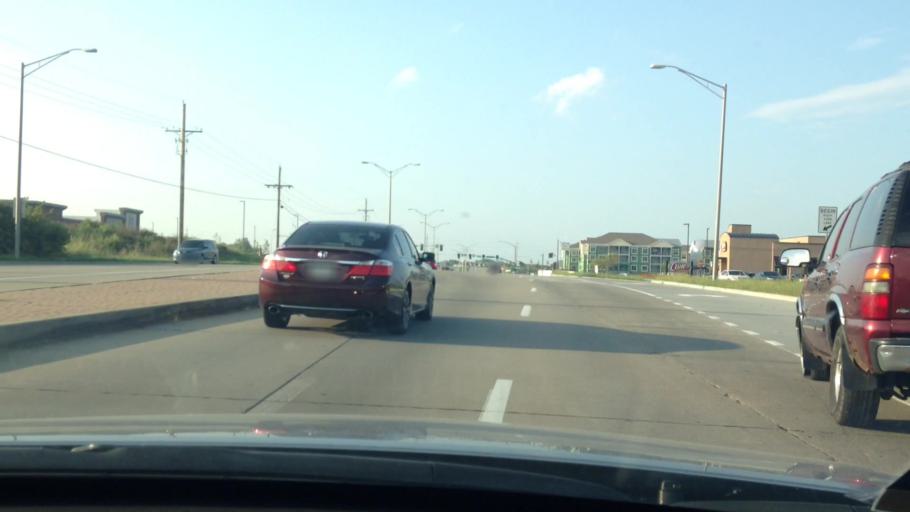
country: US
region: Missouri
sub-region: Platte County
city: Weatherby Lake
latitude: 39.2557
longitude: -94.6495
